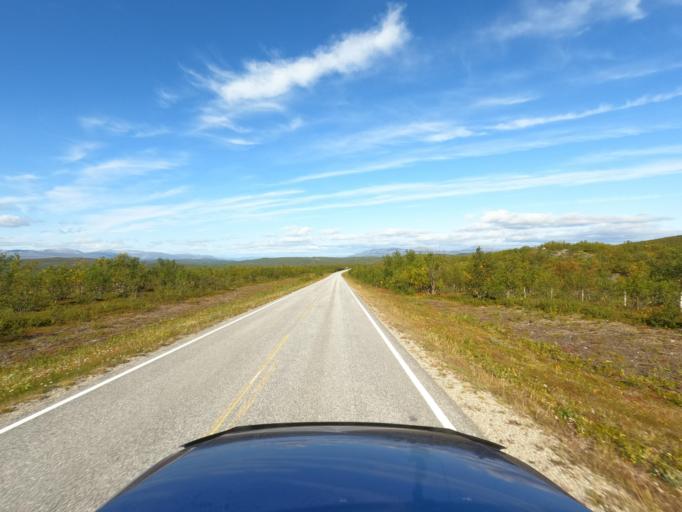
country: NO
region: Finnmark Fylke
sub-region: Karasjok
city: Karasjohka
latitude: 69.7246
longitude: 25.2363
